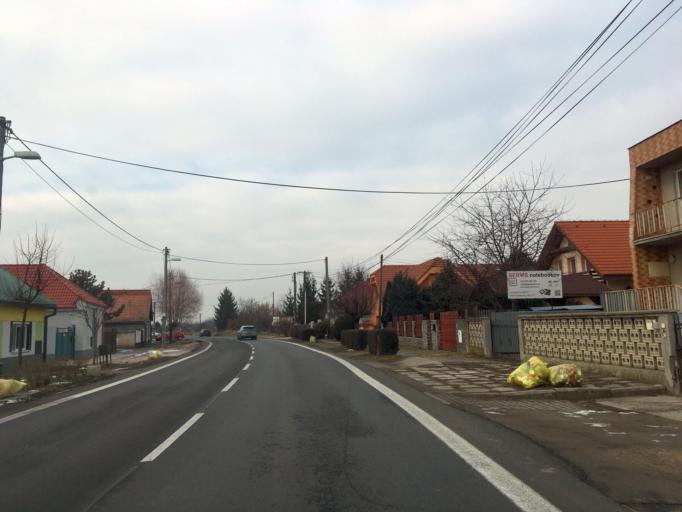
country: SK
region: Nitriansky
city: Sellye
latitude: 48.1666
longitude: 17.8831
